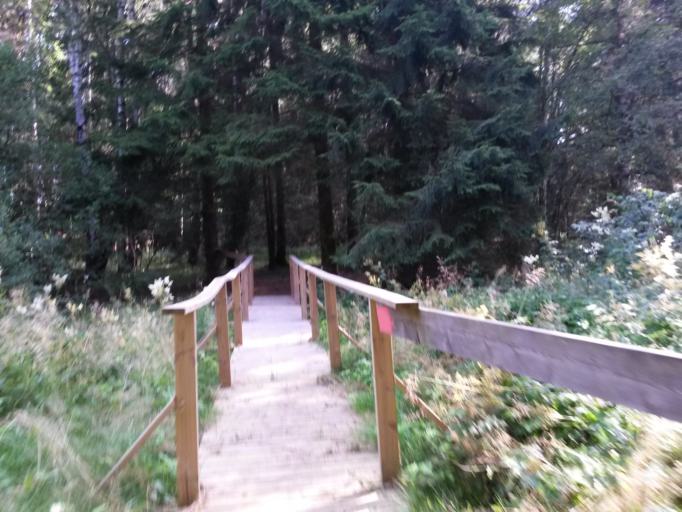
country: SE
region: Vaestra Goetaland
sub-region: Vargarda Kommun
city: Vargarda
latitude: 58.0471
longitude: 12.8211
